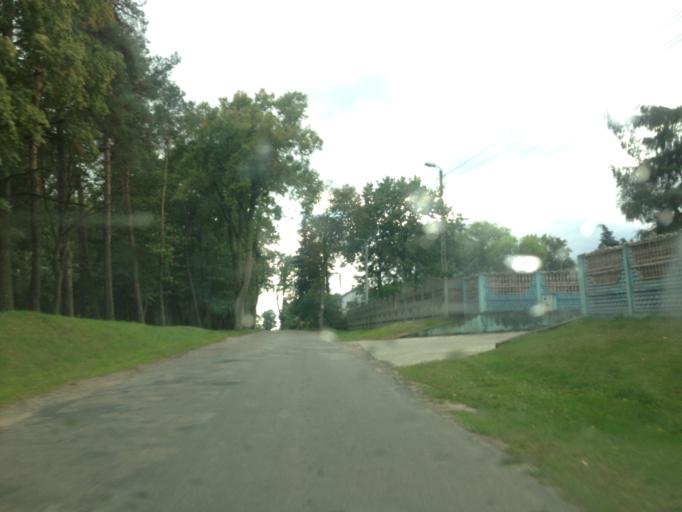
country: PL
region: Pomeranian Voivodeship
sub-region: Powiat kwidzynski
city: Prabuty
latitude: 53.7643
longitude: 19.2013
